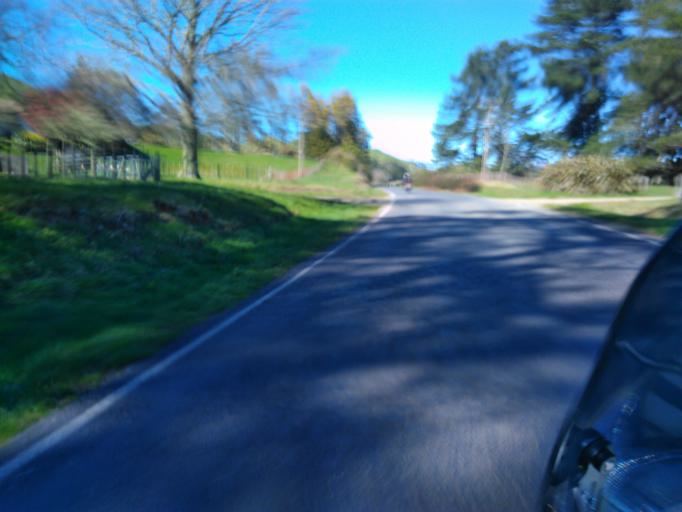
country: NZ
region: Bay of Plenty
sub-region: Opotiki District
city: Opotiki
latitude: -38.3354
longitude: 177.5332
